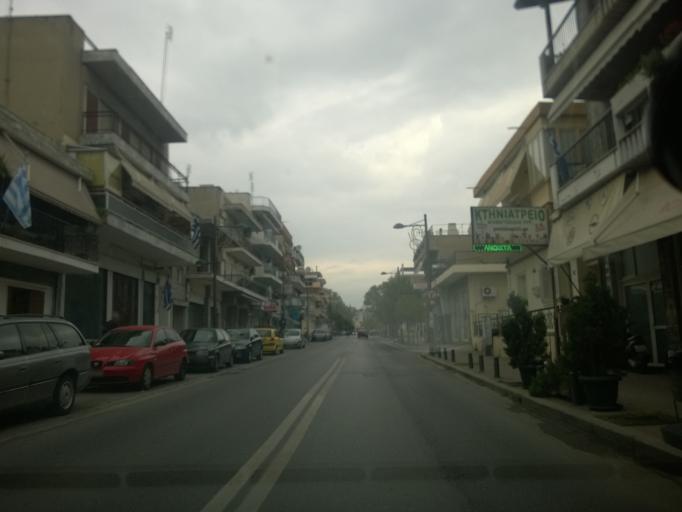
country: GR
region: Central Macedonia
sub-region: Nomos Thessalonikis
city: Stavroupoli
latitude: 40.6698
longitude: 22.9332
